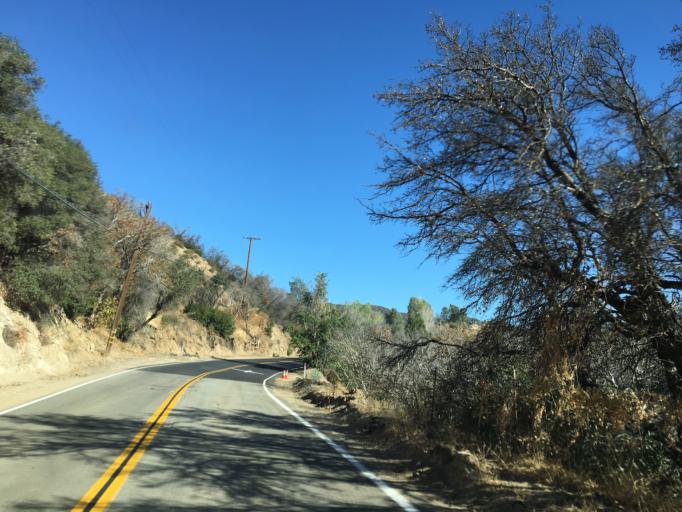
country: US
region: California
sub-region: Los Angeles County
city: Green Valley
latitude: 34.6705
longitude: -118.4548
